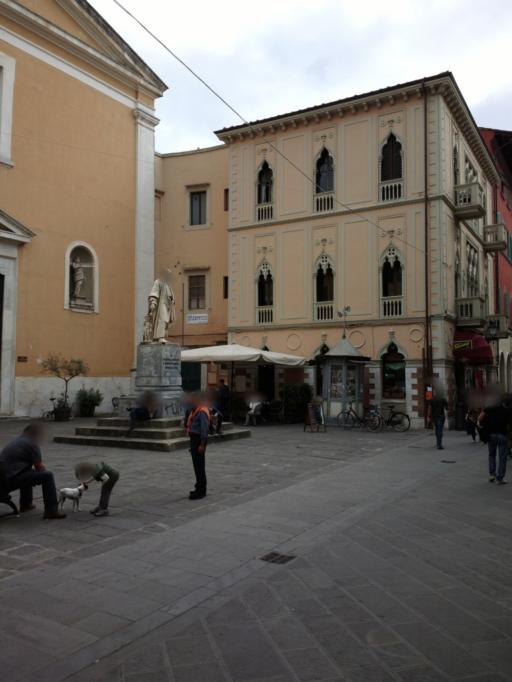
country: IT
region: Tuscany
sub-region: Province of Pisa
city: Pisa
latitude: 43.7131
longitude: 10.4002
